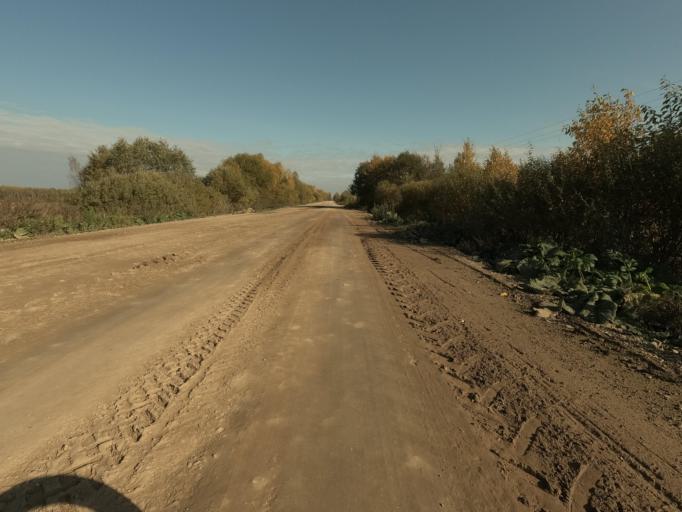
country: RU
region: Novgorod
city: Batetskiy
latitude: 58.8206
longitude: 30.7030
